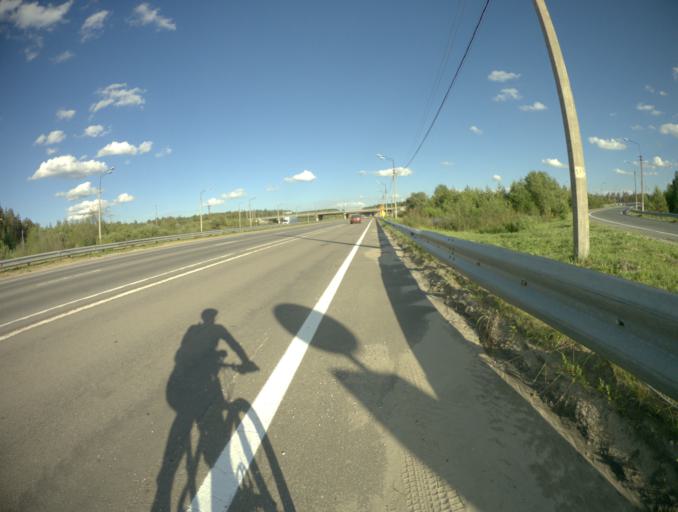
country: RU
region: Vladimir
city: Kommunar
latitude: 56.0812
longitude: 40.4696
